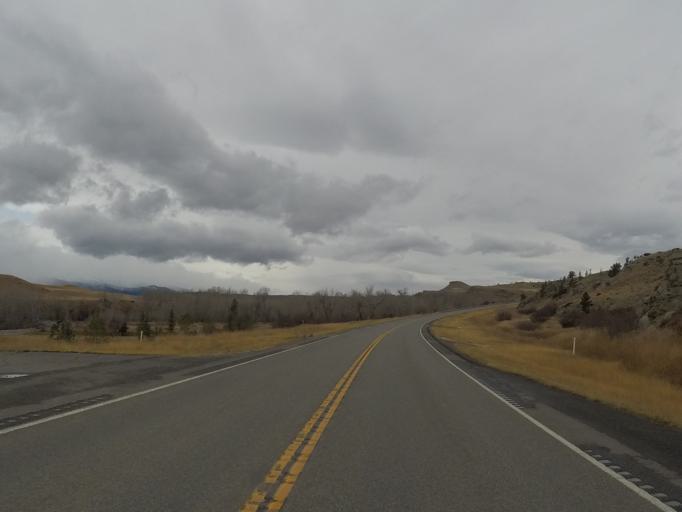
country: US
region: Montana
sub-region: Sweet Grass County
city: Big Timber
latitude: 45.9292
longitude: -109.9850
